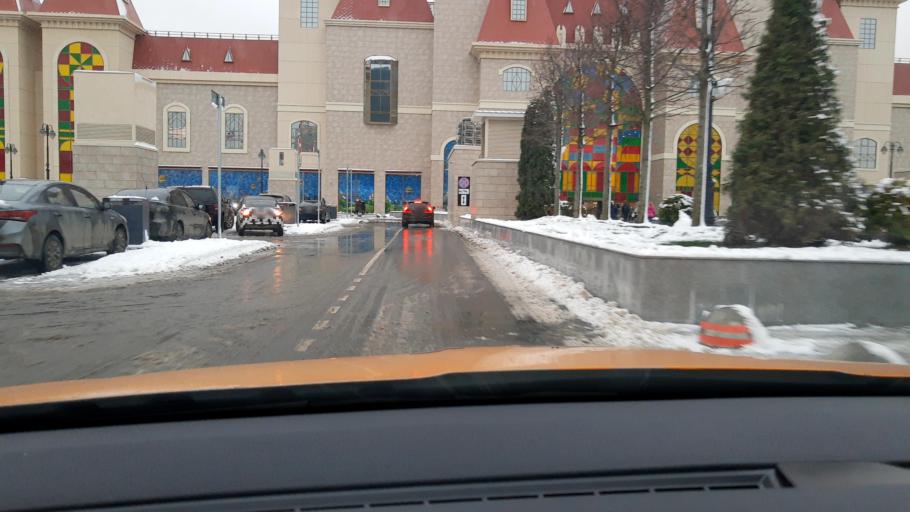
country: RU
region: Moskovskaya
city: Kozhukhovo
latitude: 55.6939
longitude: 37.6707
